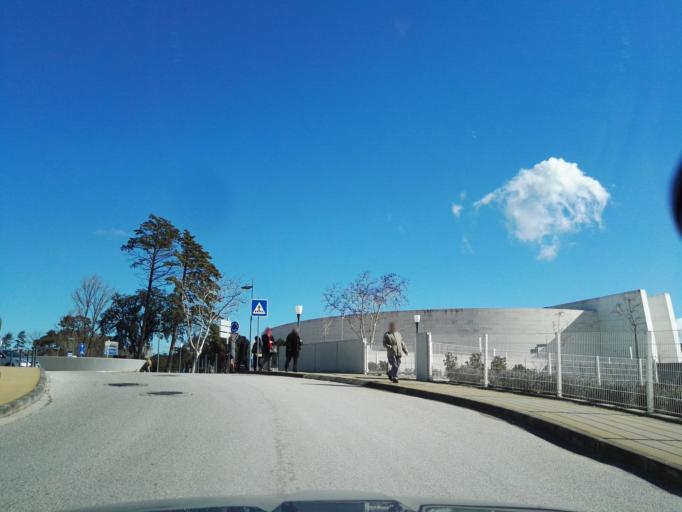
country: PT
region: Santarem
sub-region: Ourem
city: Fatima
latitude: 39.6293
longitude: -8.6781
